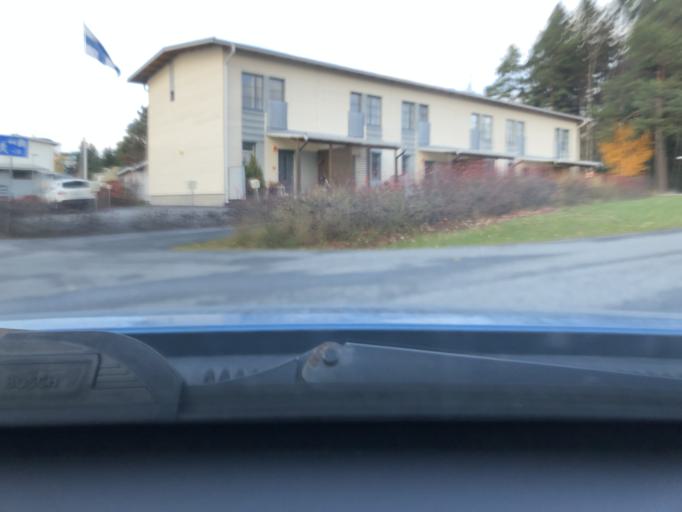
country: FI
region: Pirkanmaa
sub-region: Tampere
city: Kangasala
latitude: 61.4701
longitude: 24.0291
